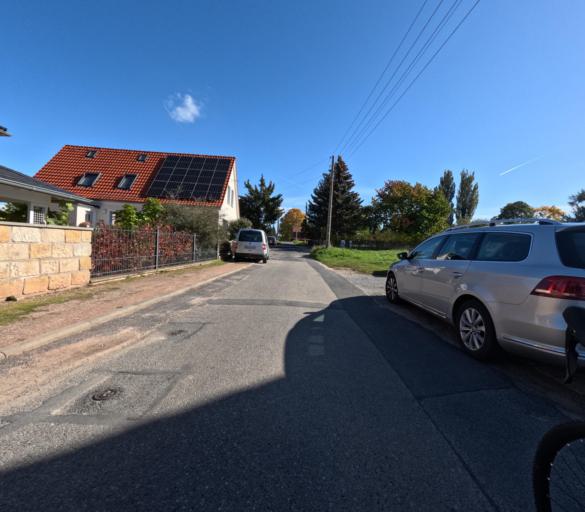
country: DE
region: Saxony
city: Radebeul
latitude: 51.1148
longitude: 13.6824
